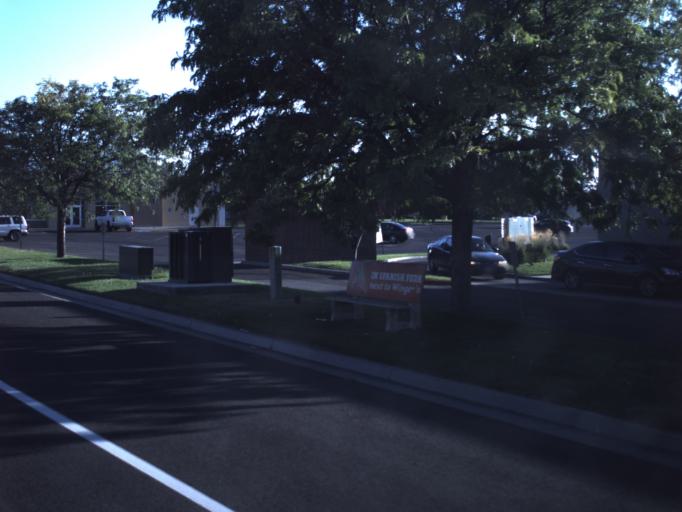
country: US
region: Utah
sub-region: Utah County
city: Spanish Fork
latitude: 40.1225
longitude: -111.6548
